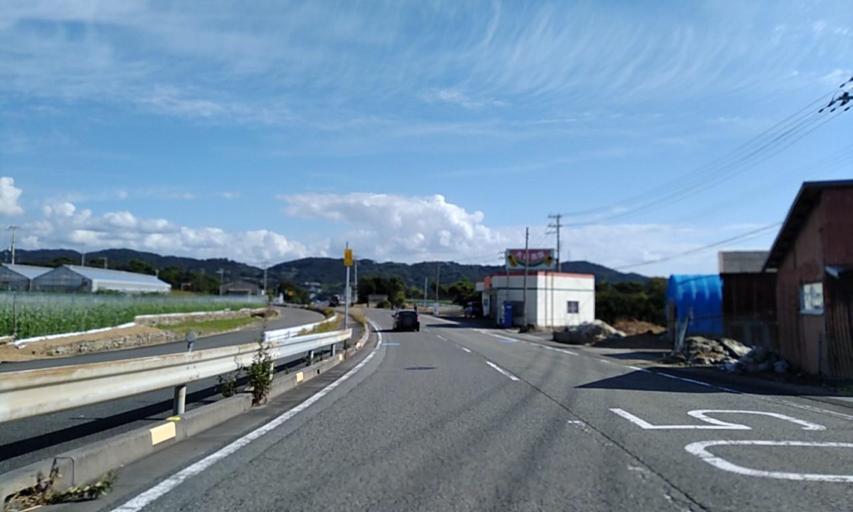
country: JP
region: Wakayama
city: Gobo
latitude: 33.8032
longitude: 135.2279
